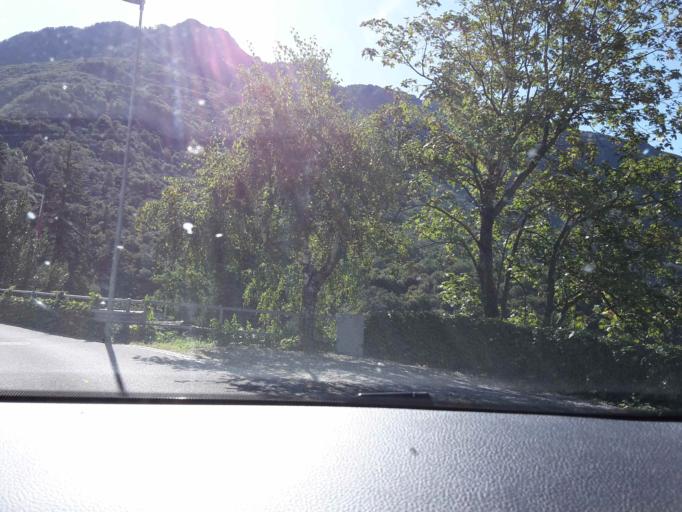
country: CH
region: Ticino
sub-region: Bellinzona District
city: Giubiasco
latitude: 46.1698
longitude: 9.0171
